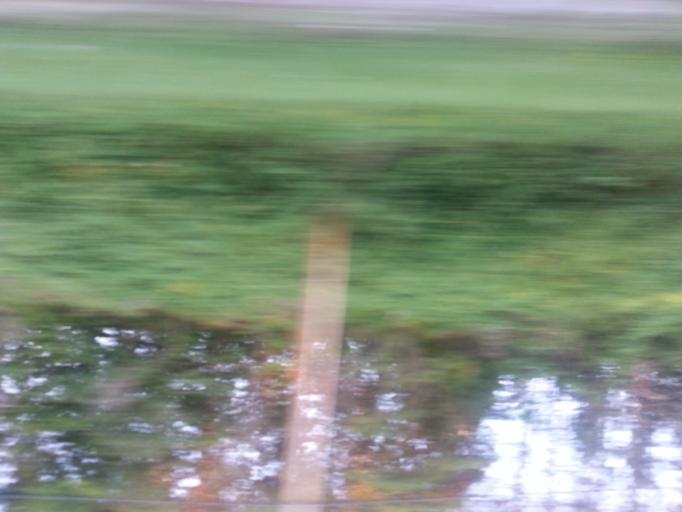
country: US
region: Tennessee
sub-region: Roane County
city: Midtown
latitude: 35.8411
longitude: -84.5424
